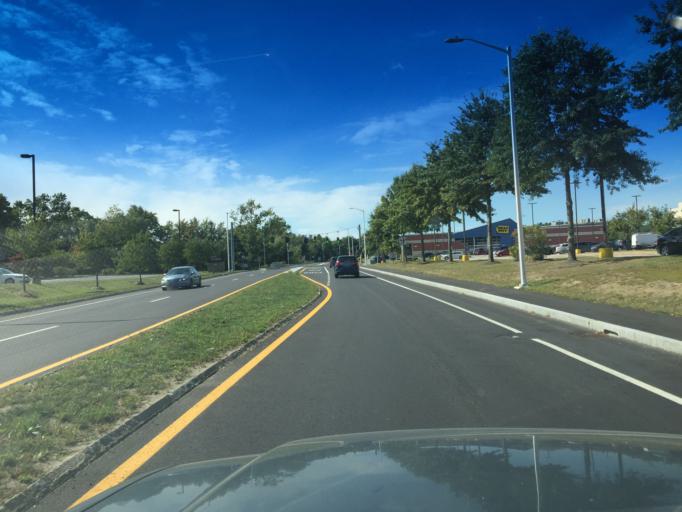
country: US
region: Massachusetts
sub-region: Worcester County
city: Berlin
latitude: 42.3528
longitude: -71.6163
